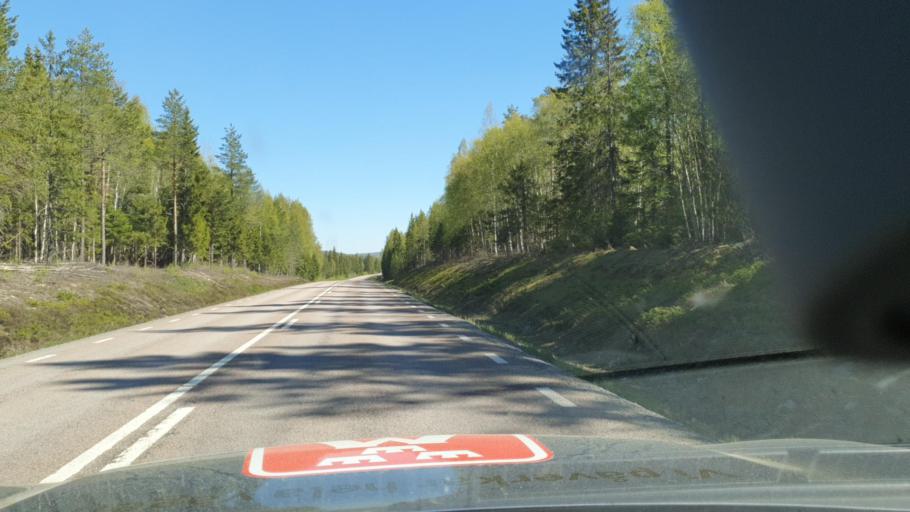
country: SE
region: Vaesternorrland
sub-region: OErnskoeldsviks Kommun
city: Ornskoldsvik
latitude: 63.4052
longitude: 18.6514
